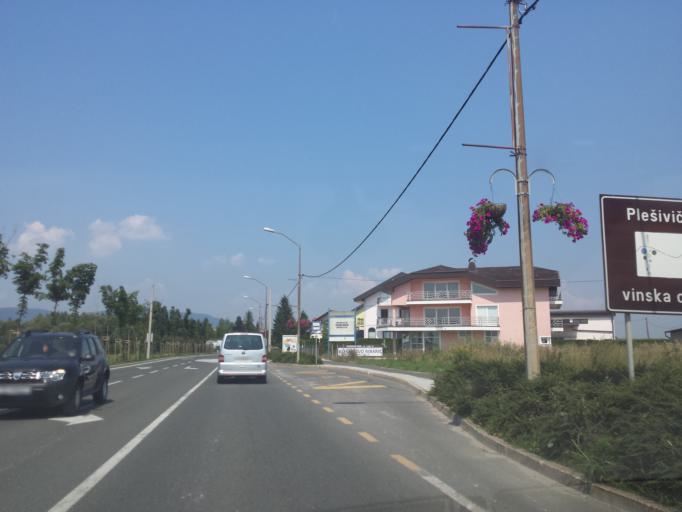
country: HR
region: Zagrebacka
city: Jastrebarsko
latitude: 45.6595
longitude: 15.6400
